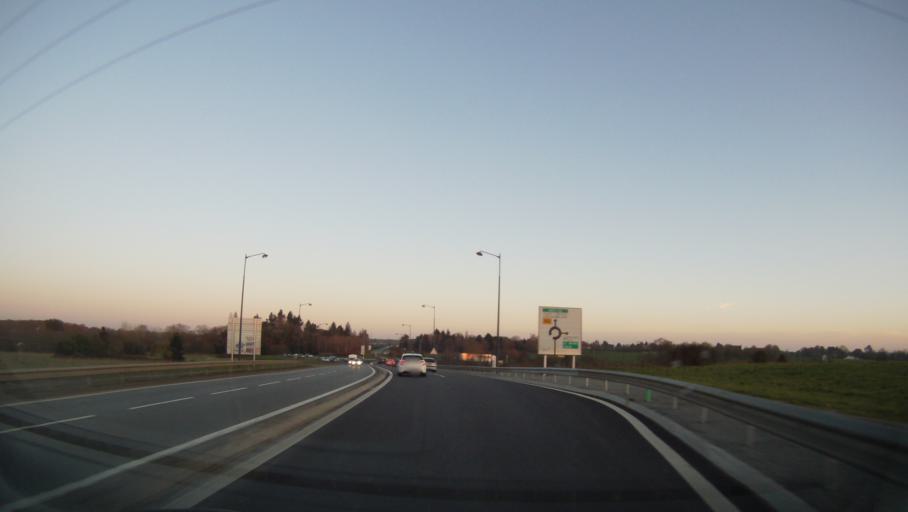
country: FR
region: Brittany
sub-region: Departement d'Ille-et-Vilaine
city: Chantepie
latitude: 48.0834
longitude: -1.6428
